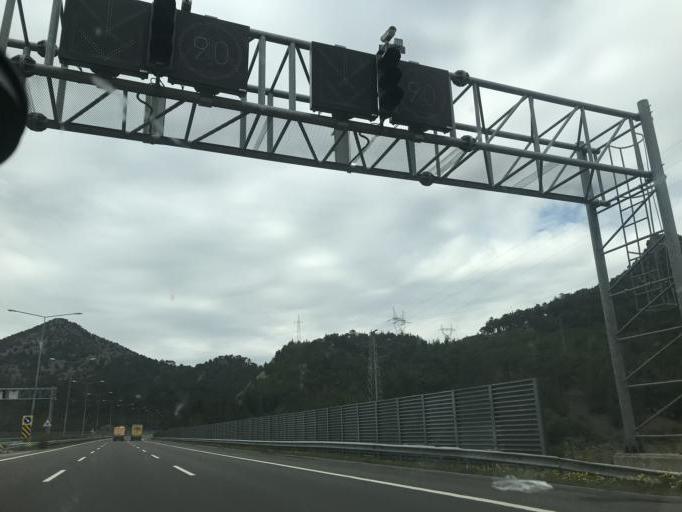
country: TR
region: Nigde
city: Ciftehan
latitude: 37.5022
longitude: 34.8241
